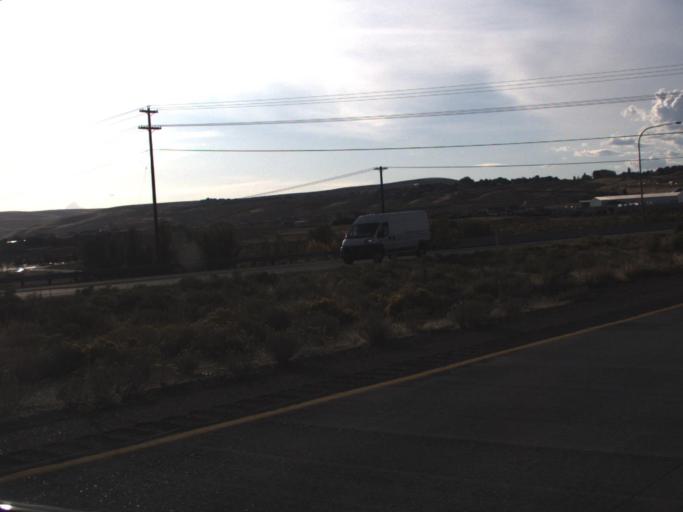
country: US
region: Washington
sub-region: Benton County
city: Richland
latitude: 46.1936
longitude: -119.2666
